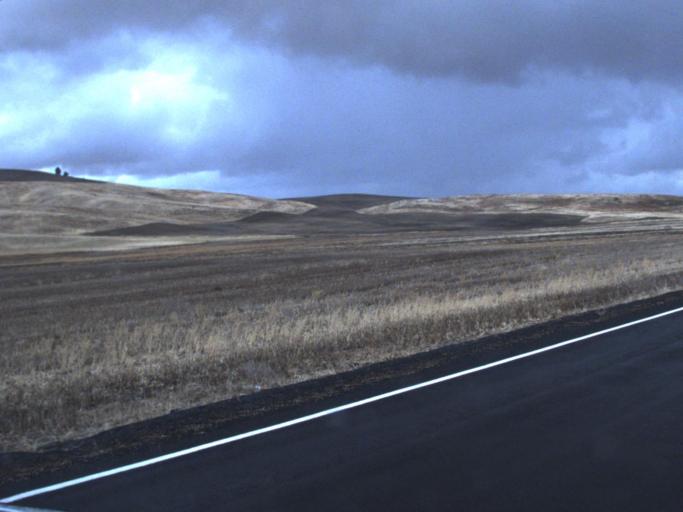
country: US
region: Washington
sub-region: Spokane County
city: Medical Lake
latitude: 47.6974
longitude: -117.8796
